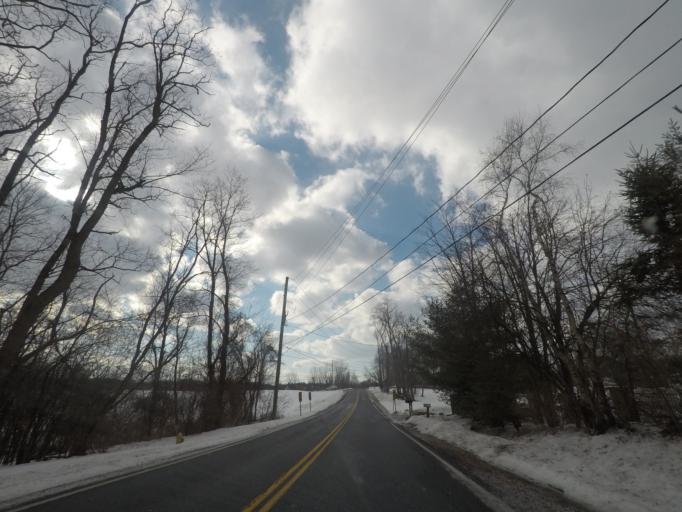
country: US
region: New York
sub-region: Saratoga County
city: Mechanicville
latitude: 42.8967
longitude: -73.7474
